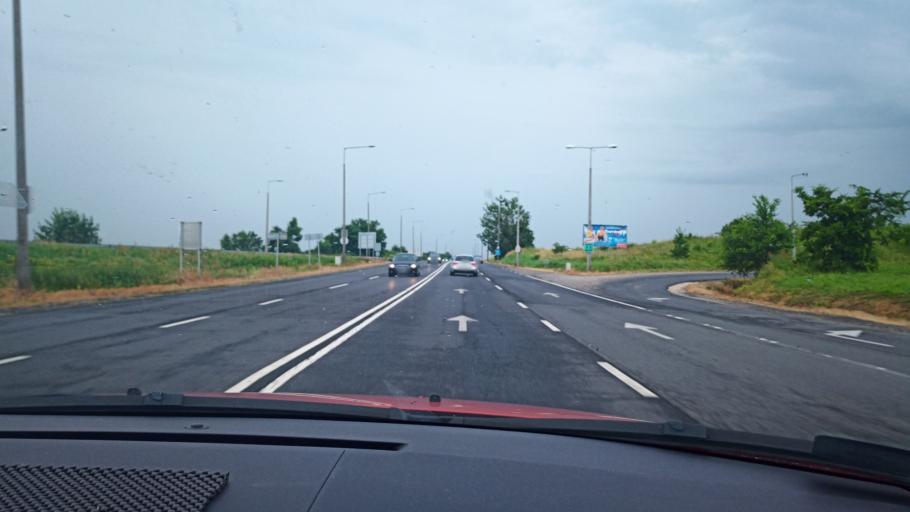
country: HU
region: Borsod-Abauj-Zemplen
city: Malyi
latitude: 48.0520
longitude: 20.7988
